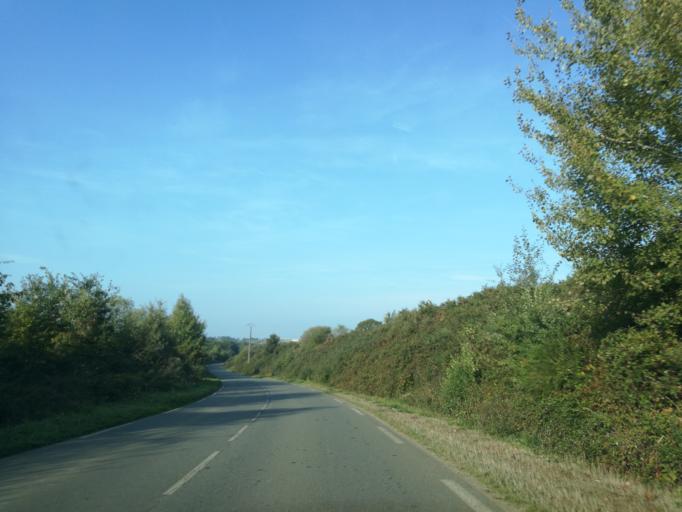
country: FR
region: Brittany
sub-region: Departement d'Ille-et-Vilaine
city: Pleumeleuc
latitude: 48.1697
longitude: -1.9004
